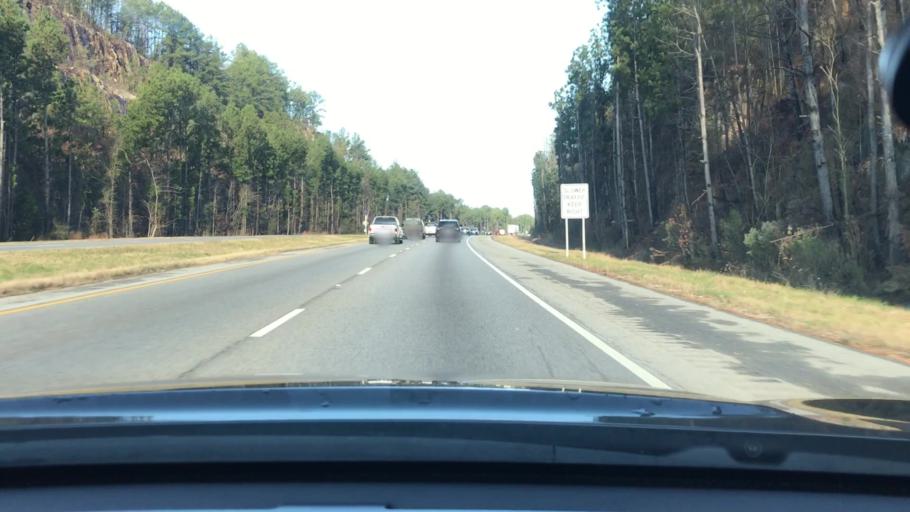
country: US
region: Alabama
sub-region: Shelby County
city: Chelsea
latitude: 33.3578
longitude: -86.6531
